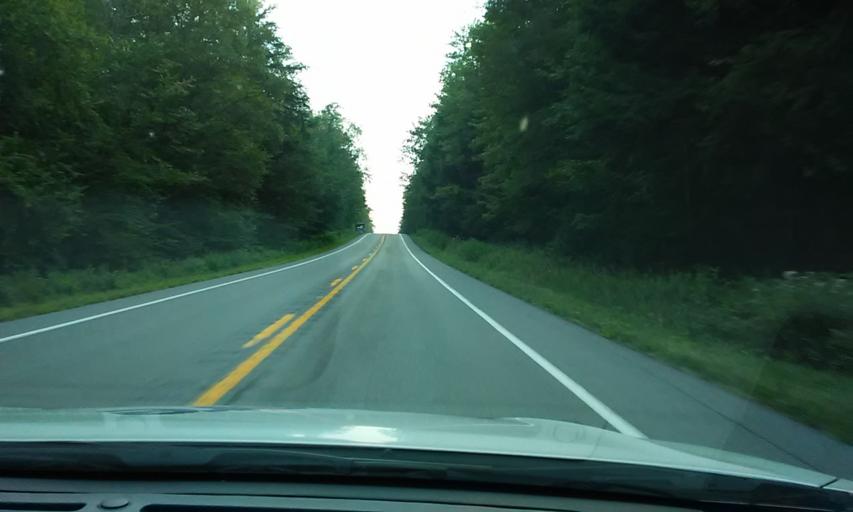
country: US
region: Pennsylvania
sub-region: Warren County
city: Sheffield
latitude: 41.5618
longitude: -78.9904
